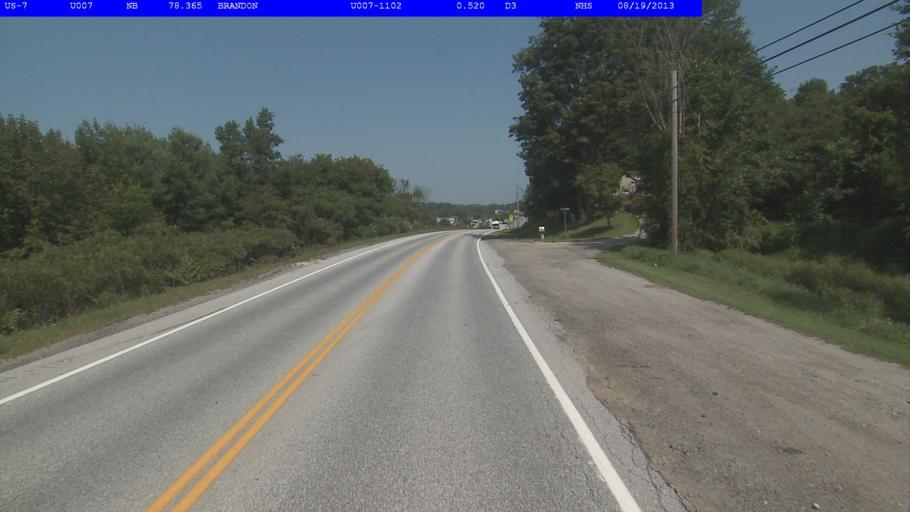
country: US
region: Vermont
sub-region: Rutland County
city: Brandon
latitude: 43.7617
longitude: -73.0497
